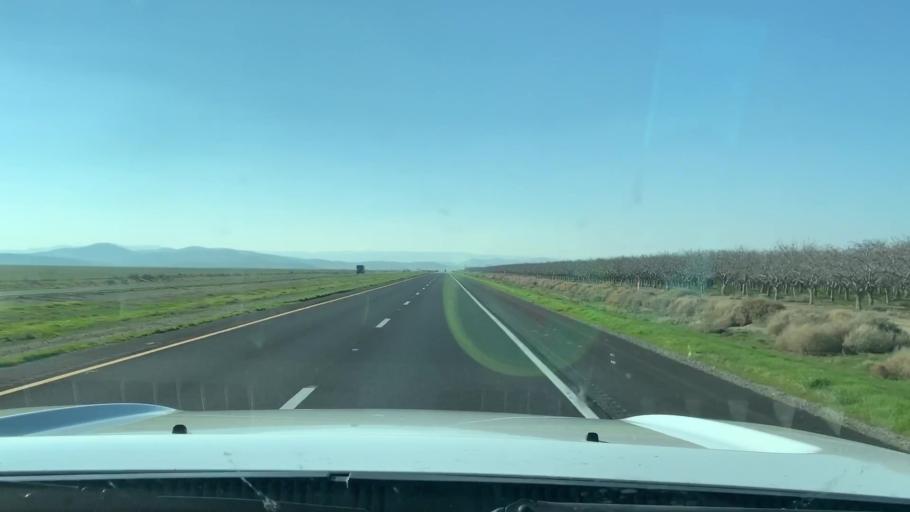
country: US
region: California
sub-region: Kern County
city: Lost Hills
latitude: 35.6148
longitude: -119.9407
